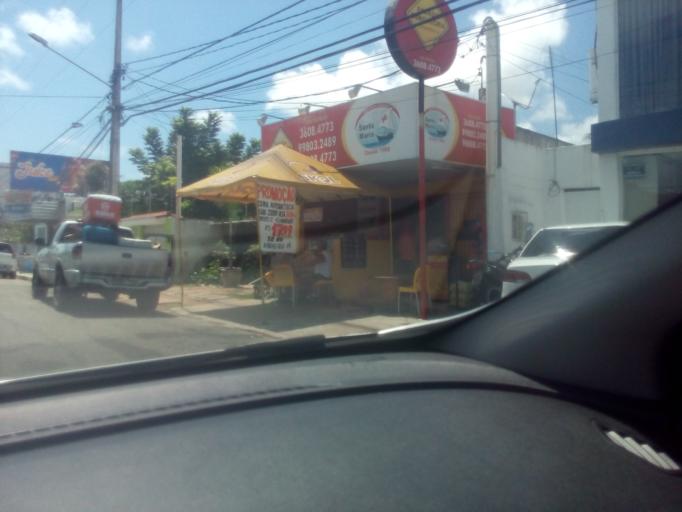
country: BR
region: Rio Grande do Norte
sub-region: Parnamirim
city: Parnamirim
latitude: -5.8822
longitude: -35.2042
